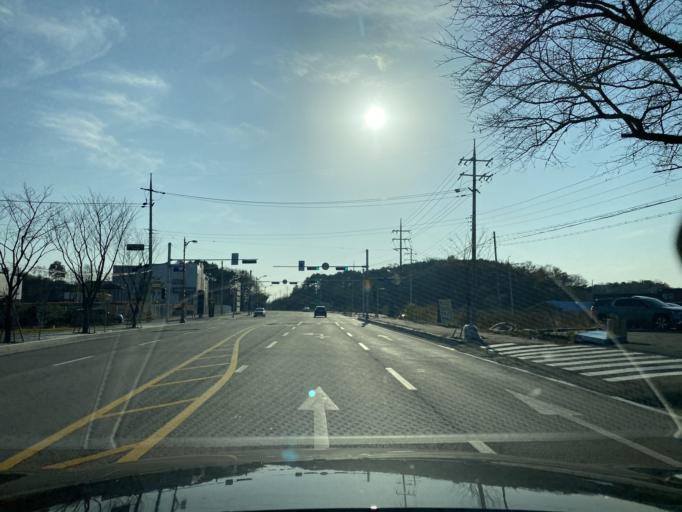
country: KR
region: Chungcheongnam-do
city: Yesan
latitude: 36.7188
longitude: 126.8453
